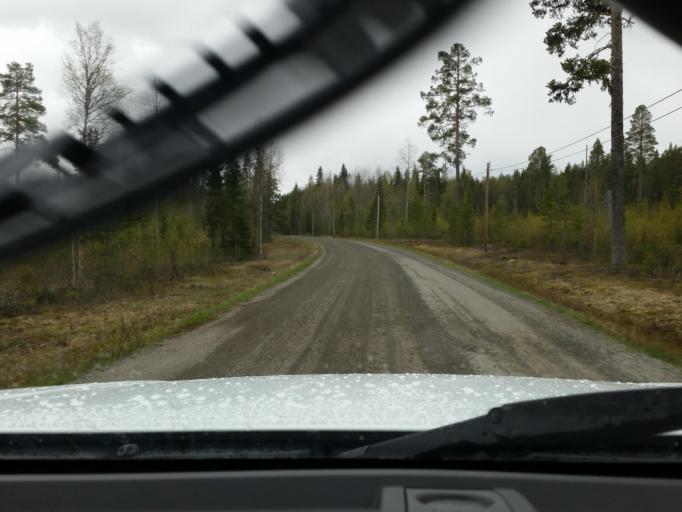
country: SE
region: Norrbotten
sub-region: Pitea Kommun
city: Norrfjarden
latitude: 65.5649
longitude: 21.4805
